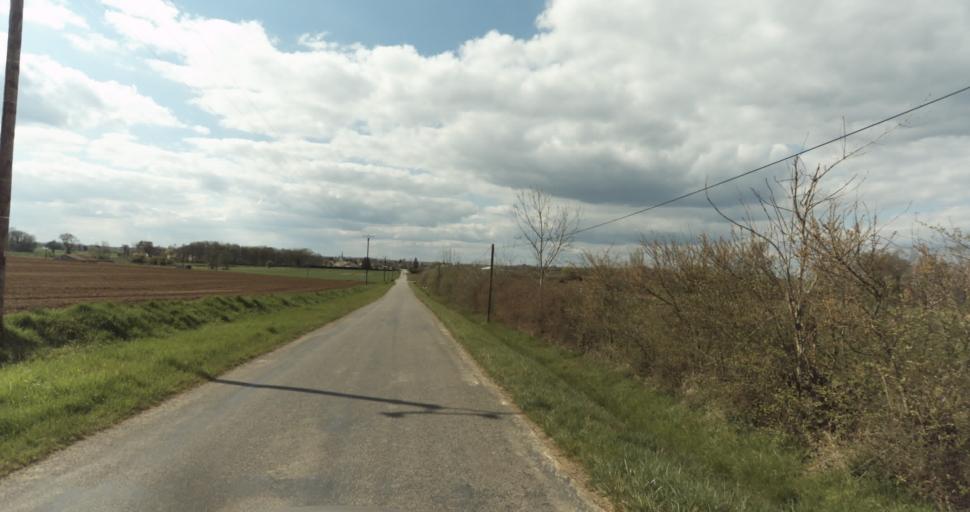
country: FR
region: Bourgogne
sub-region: Departement de la Cote-d'Or
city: Auxonne
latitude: 47.1885
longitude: 5.4227
